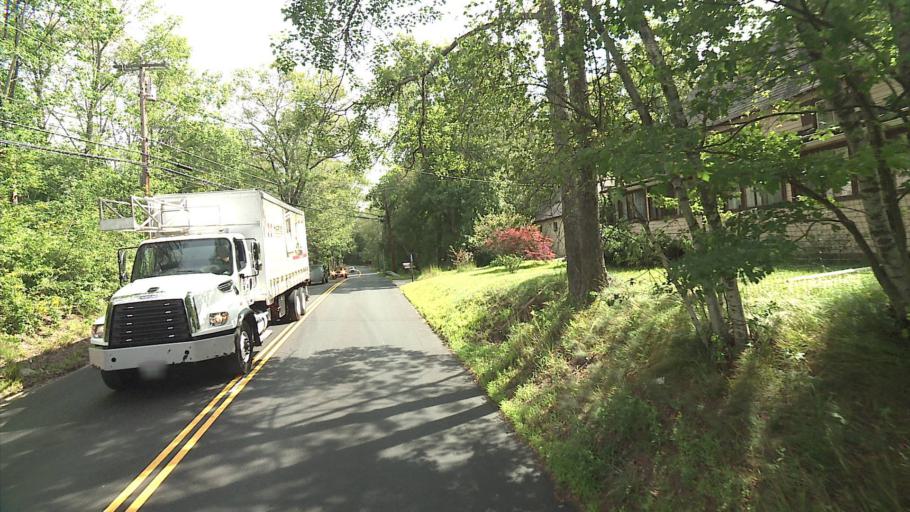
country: US
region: Connecticut
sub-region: Windham County
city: South Woodstock
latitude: 41.9452
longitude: -72.0649
